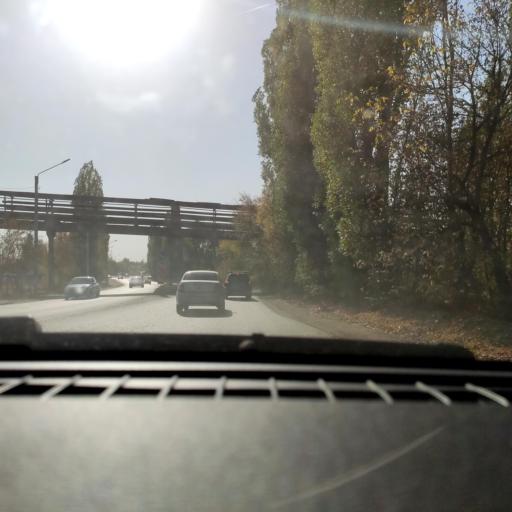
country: RU
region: Voronezj
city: Maslovka
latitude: 51.6252
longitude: 39.2610
